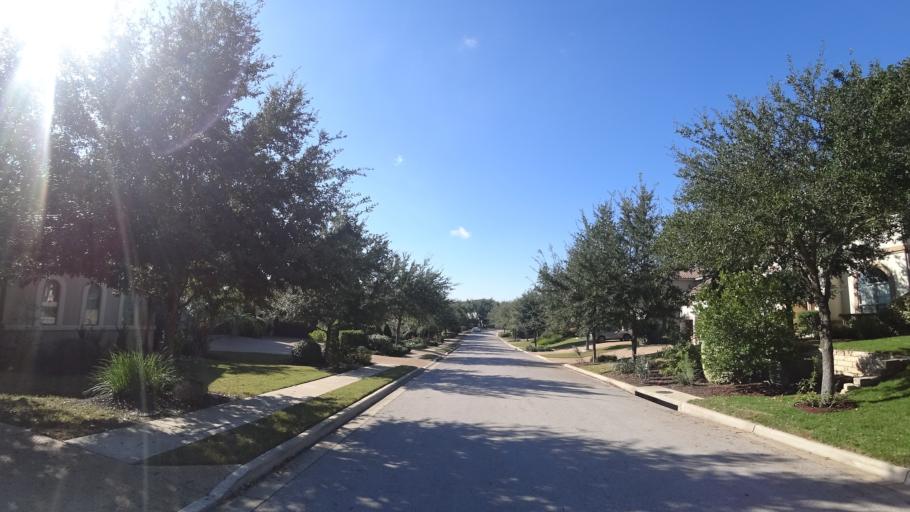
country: US
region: Texas
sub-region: Travis County
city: Bee Cave
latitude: 30.3532
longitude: -97.8926
